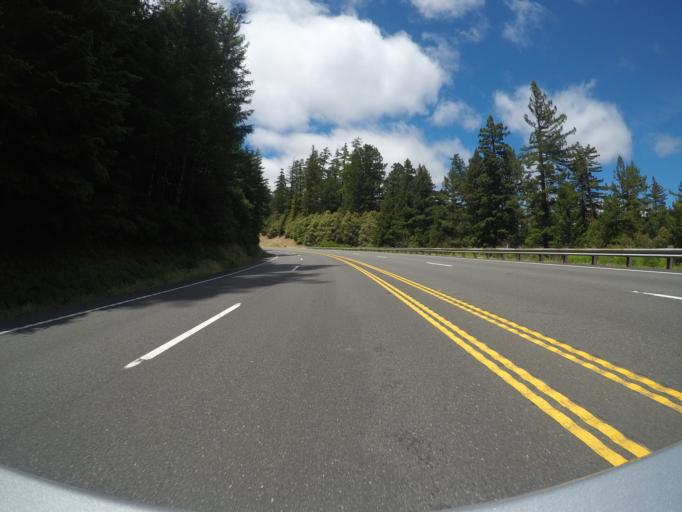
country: US
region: California
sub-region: Humboldt County
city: Redway
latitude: 40.2706
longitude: -123.8529
